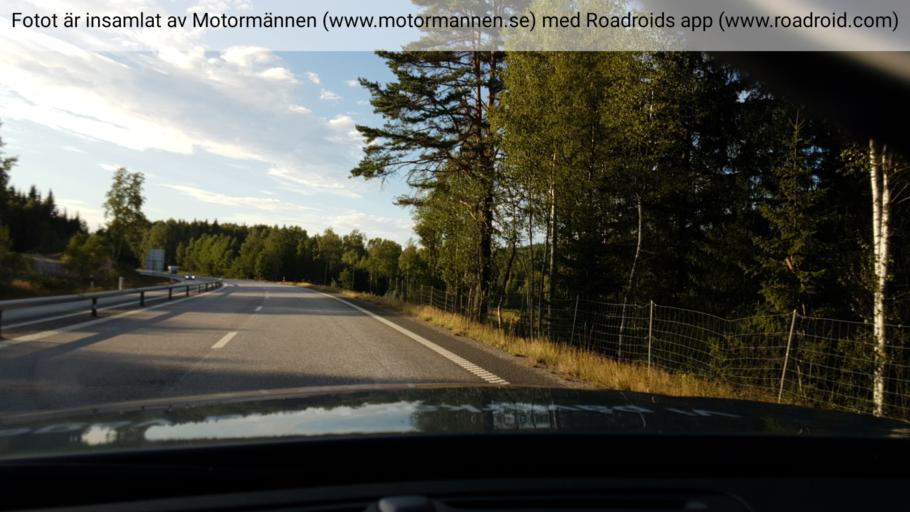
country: SE
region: OErebro
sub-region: Lekebergs Kommun
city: Fjugesta
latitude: 59.2596
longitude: 14.8110
